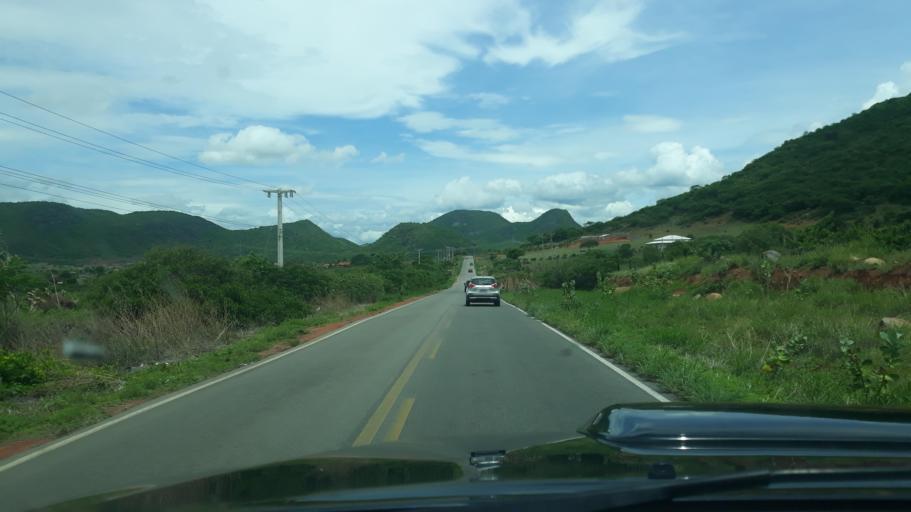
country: BR
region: Bahia
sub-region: Guanambi
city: Guanambi
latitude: -14.2580
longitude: -42.7300
